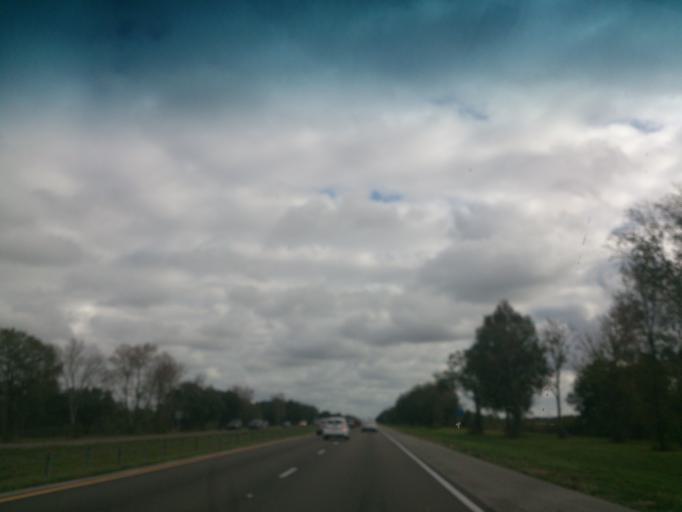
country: US
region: Florida
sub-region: Orange County
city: Wedgefield
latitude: 28.4516
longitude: -81.0915
